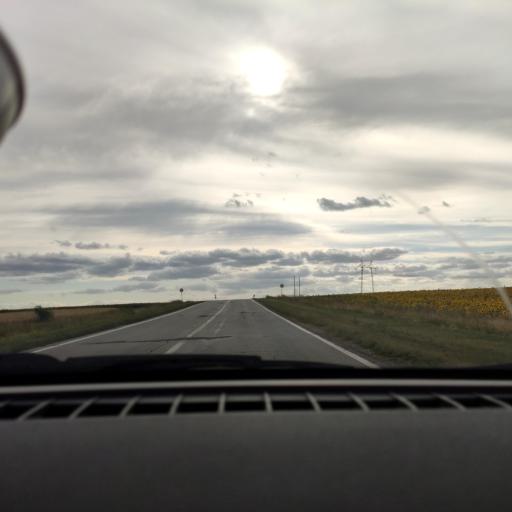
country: RU
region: Samara
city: Krasnyy Yar
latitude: 53.4415
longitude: 50.5997
